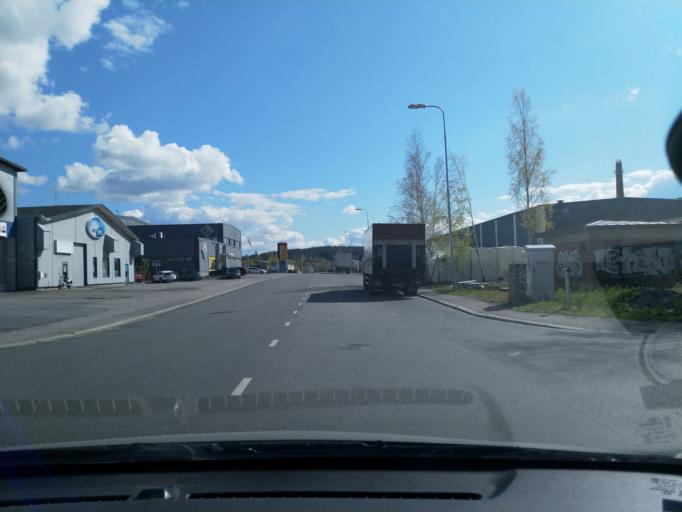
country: FI
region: Pirkanmaa
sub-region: Tampere
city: Tampere
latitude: 61.4797
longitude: 23.7896
